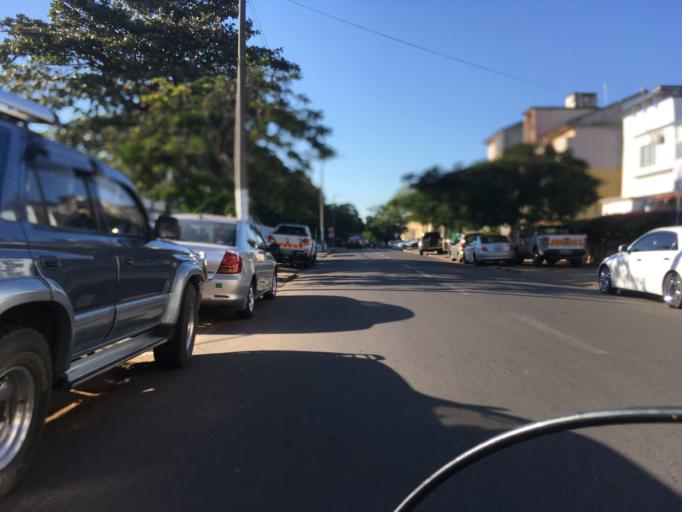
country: MZ
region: Maputo City
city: Maputo
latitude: -25.9658
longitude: 32.5875
